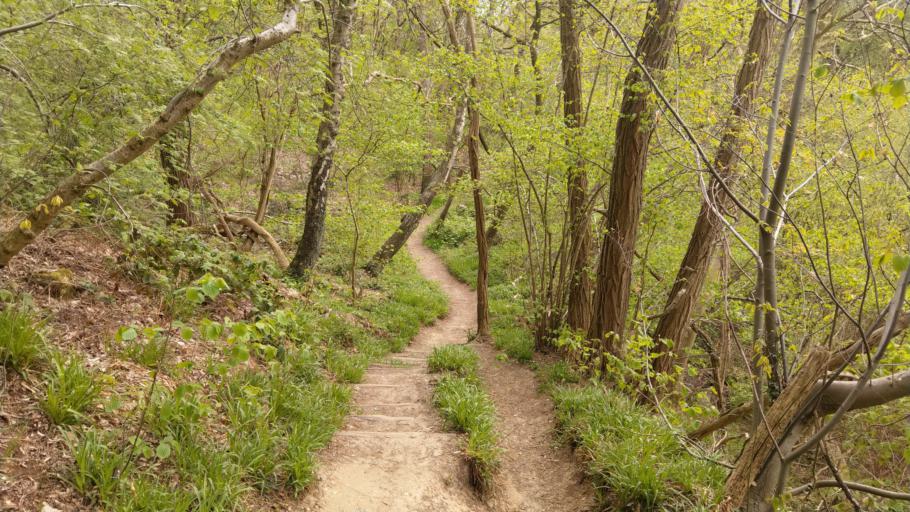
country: NL
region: Limburg
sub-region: Gemeente Meerssen
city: Meerssen
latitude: 50.9109
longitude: 5.7442
